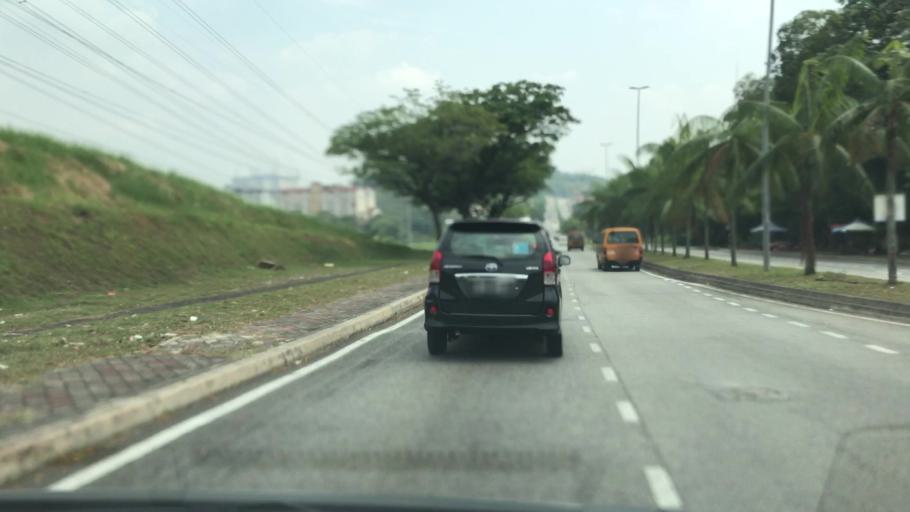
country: MY
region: Selangor
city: Kampong Baharu Balakong
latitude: 3.0309
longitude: 101.6799
